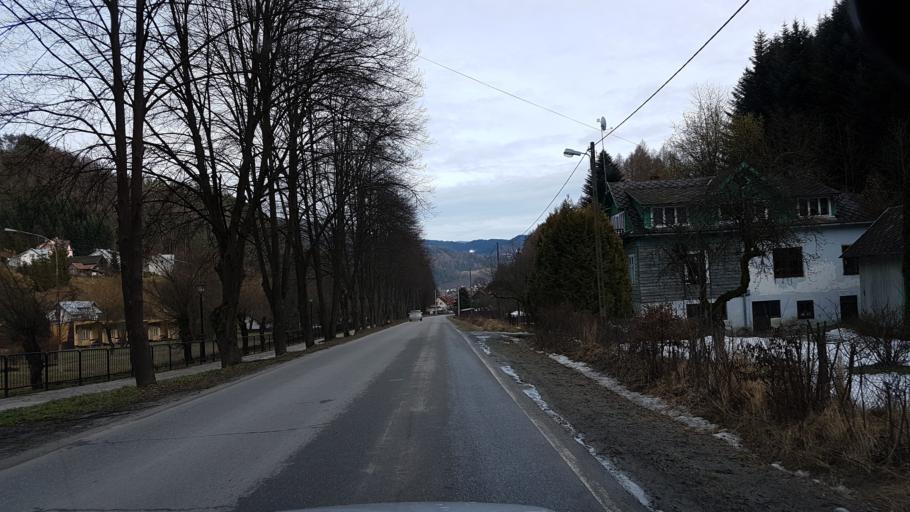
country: PL
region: Lesser Poland Voivodeship
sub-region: Powiat nowosadecki
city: Piwniczna-Zdroj
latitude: 49.4362
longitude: 20.6956
